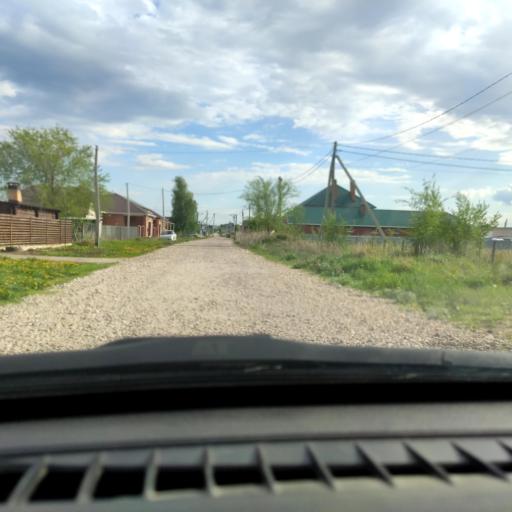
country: RU
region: Samara
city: Tol'yatti
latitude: 53.5675
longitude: 49.4081
